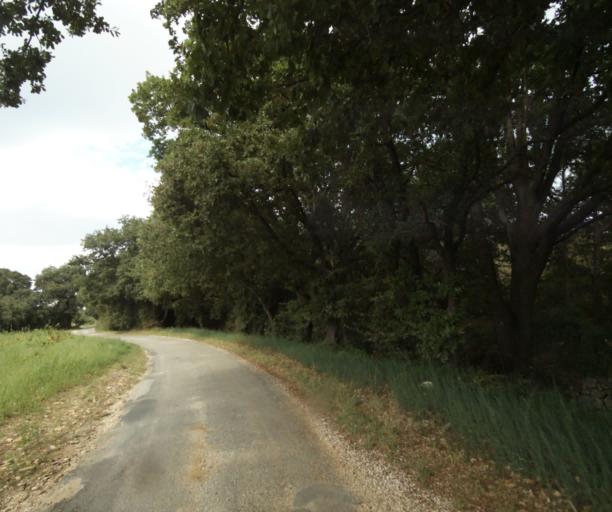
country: FR
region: Languedoc-Roussillon
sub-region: Departement des Pyrenees-Orientales
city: Argelers
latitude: 42.5367
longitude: 3.0235
